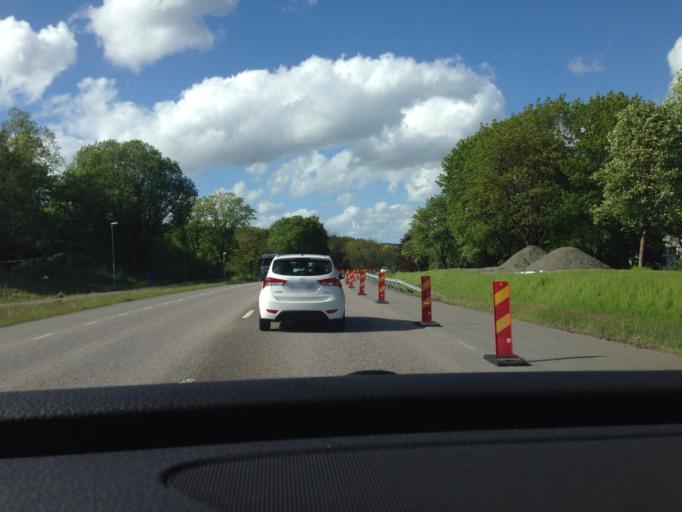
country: SE
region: Vaestra Goetaland
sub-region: Skovde Kommun
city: Skoevde
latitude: 58.3877
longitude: 13.8329
